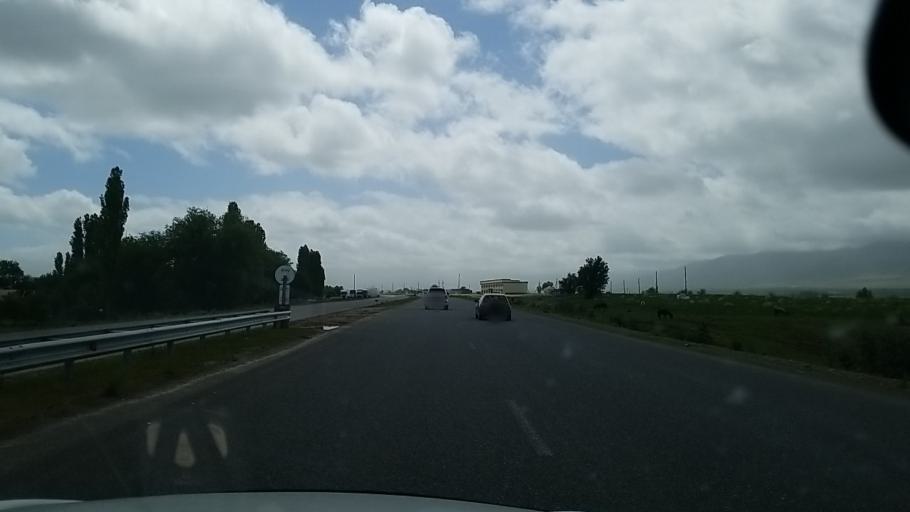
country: KZ
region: Ongtustik Qazaqstan
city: Turar Ryskulov
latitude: 42.5300
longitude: 70.3016
